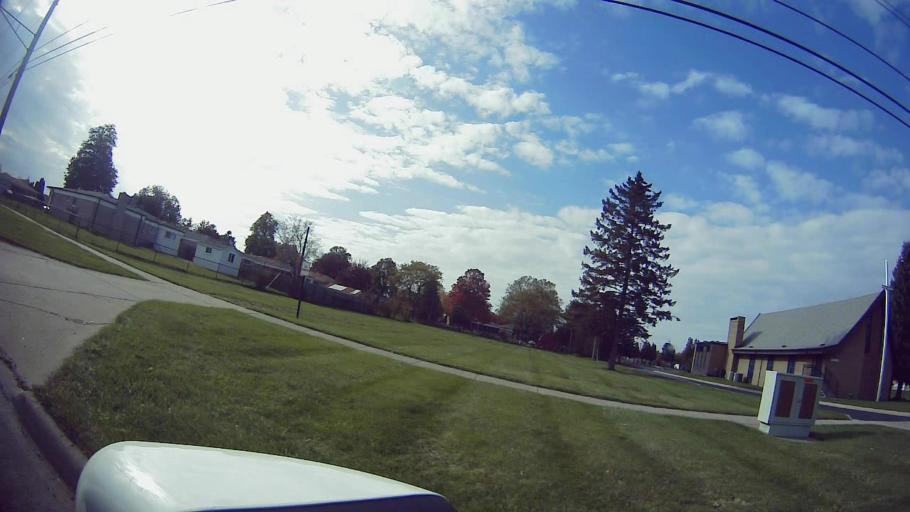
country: US
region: Michigan
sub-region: Oakland County
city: Madison Heights
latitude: 42.5327
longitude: -83.0686
